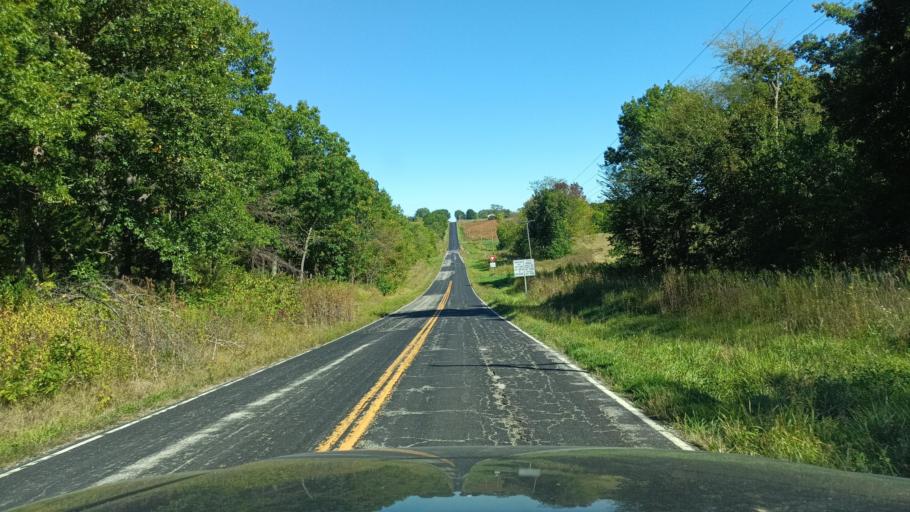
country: US
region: Missouri
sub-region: Macon County
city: La Plata
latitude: 39.9284
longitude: -92.5848
